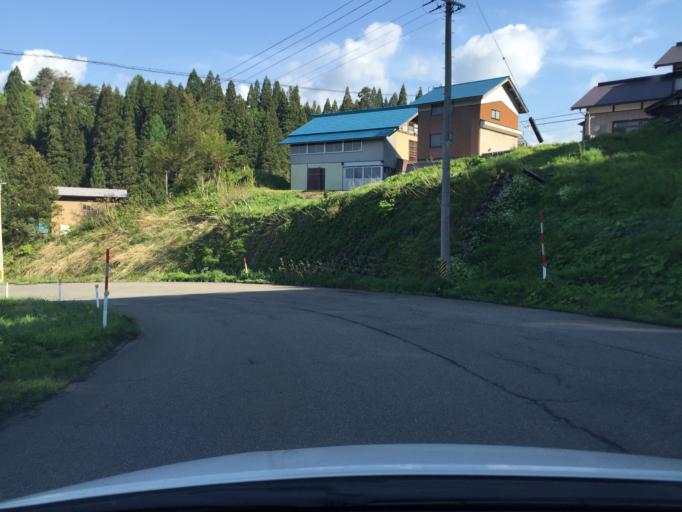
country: JP
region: Fukushima
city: Kitakata
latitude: 37.6837
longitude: 139.6845
